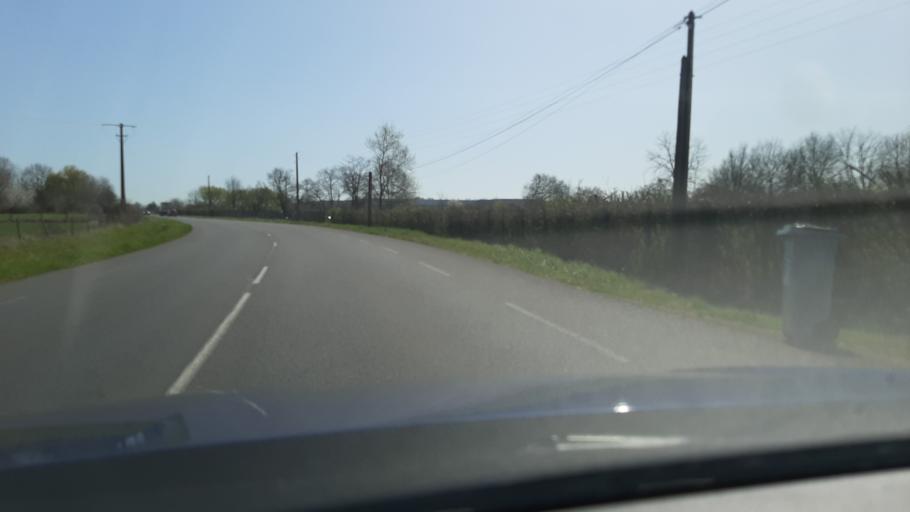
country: FR
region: Pays de la Loire
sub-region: Departement de Maine-et-Loire
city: Ecouflant
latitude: 47.5224
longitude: -0.4970
